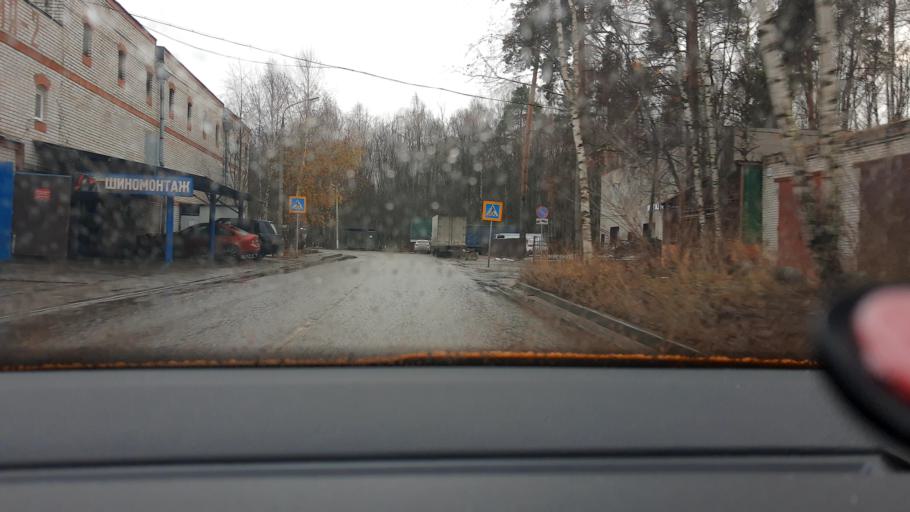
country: RU
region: Moskovskaya
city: Bolshevo
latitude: 55.9297
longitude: 37.8266
